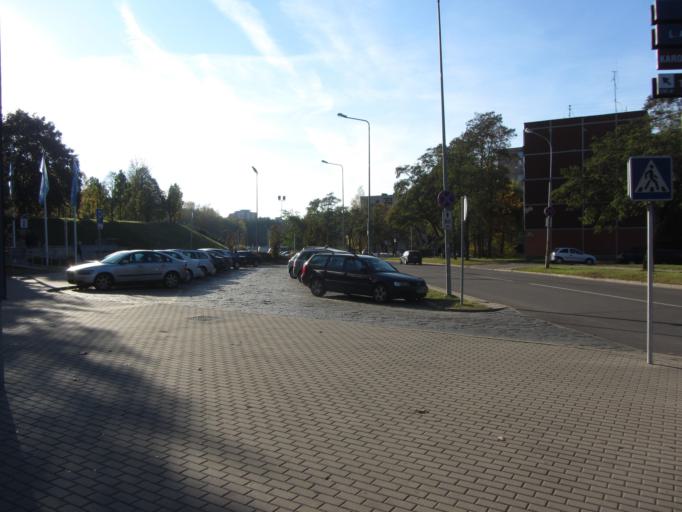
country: LT
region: Vilnius County
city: Lazdynai
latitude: 54.6886
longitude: 25.2149
